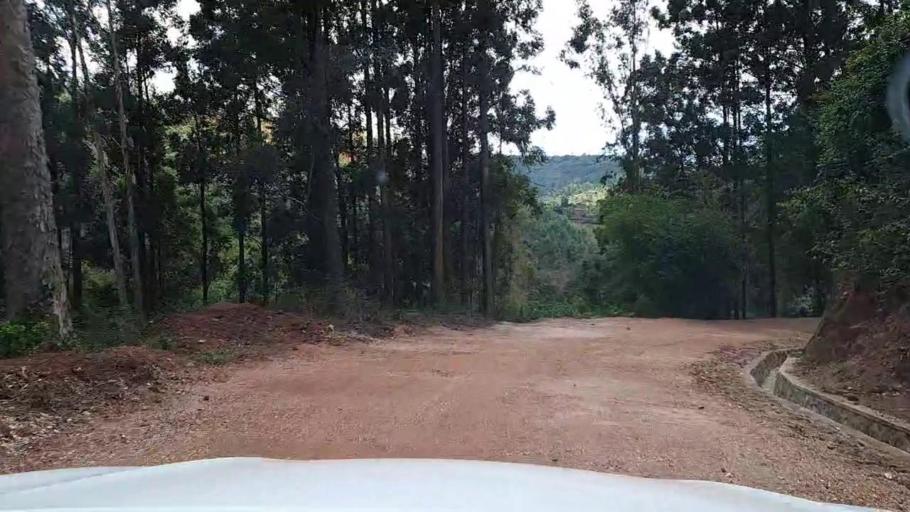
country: BI
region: Ngozi
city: Ngozi
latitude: -2.8128
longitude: 29.7296
